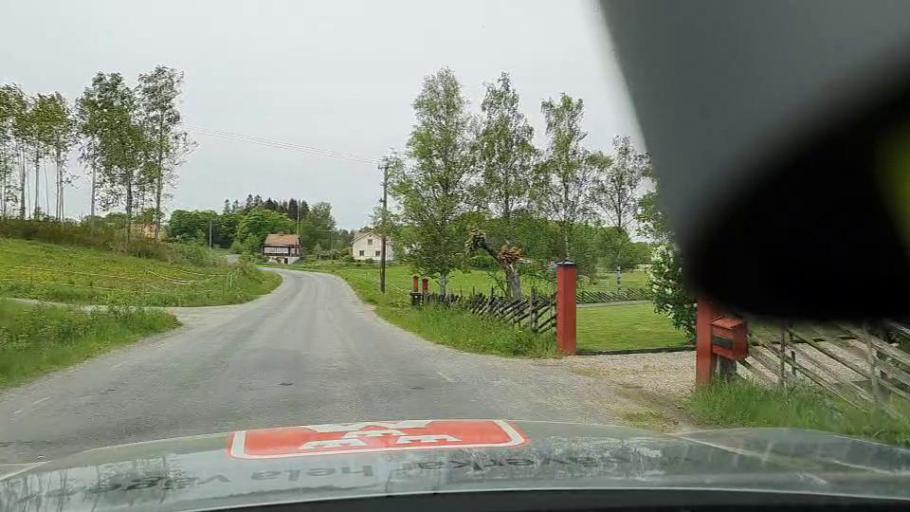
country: SE
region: Soedermanland
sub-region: Flens Kommun
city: Flen
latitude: 59.1024
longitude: 16.5514
